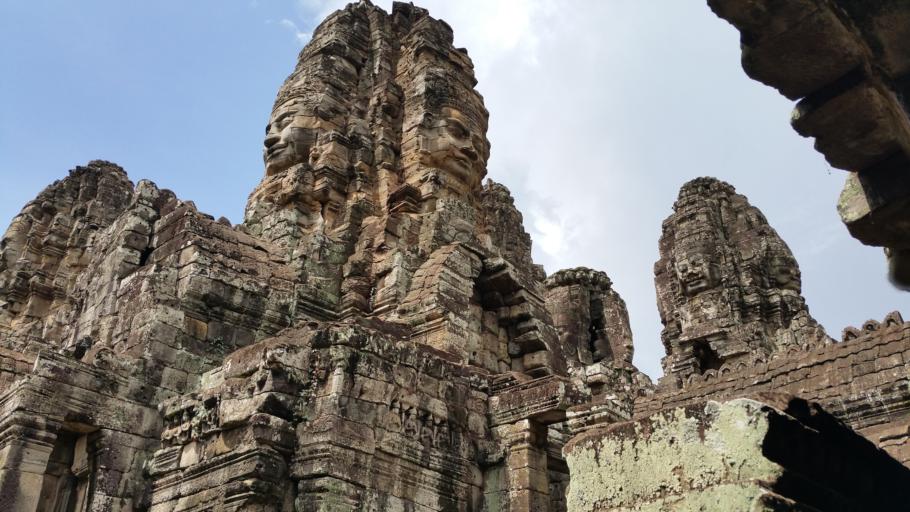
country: KH
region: Siem Reap
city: Siem Reap
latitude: 13.4411
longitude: 103.8583
